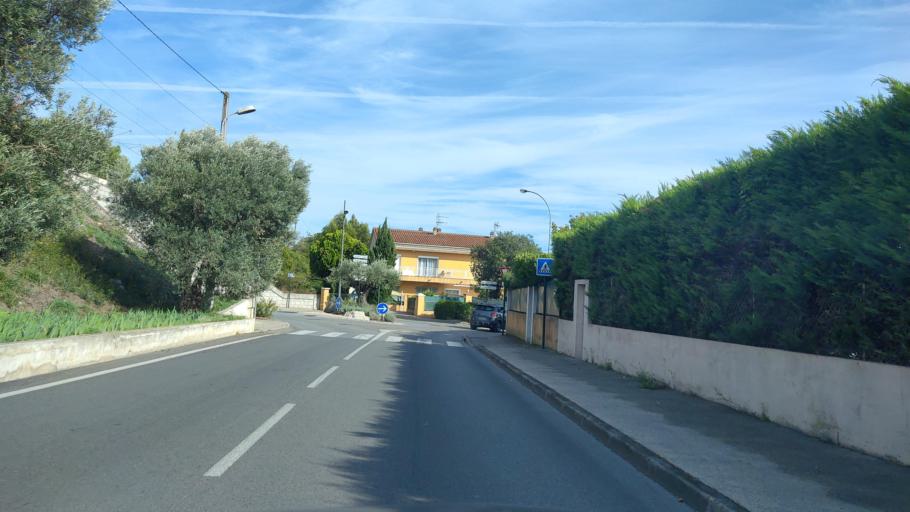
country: FR
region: Provence-Alpes-Cote d'Azur
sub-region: Departement du Var
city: Sanary-sur-Mer
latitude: 43.1262
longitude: 5.8005
